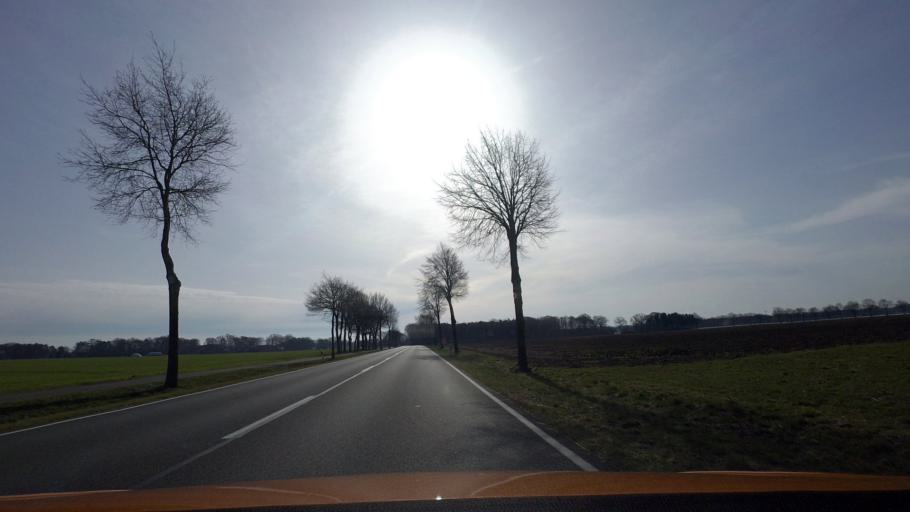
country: DE
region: Lower Saxony
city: Uchte
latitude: 52.4735
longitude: 8.9010
